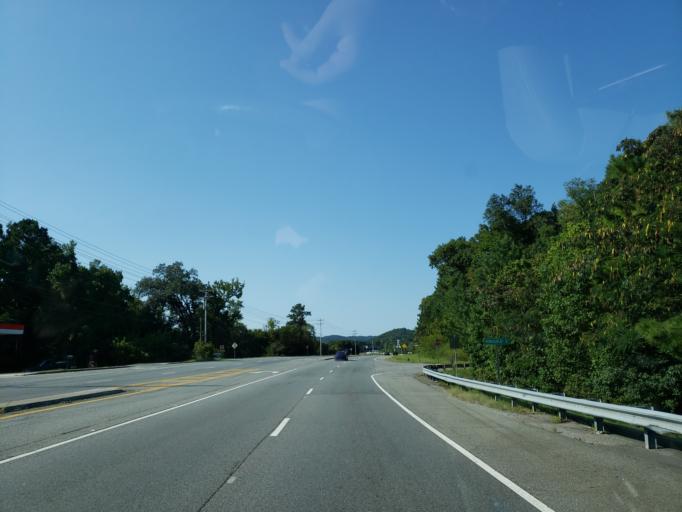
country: US
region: Georgia
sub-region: Catoosa County
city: Ringgold
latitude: 34.8945
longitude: -85.0753
